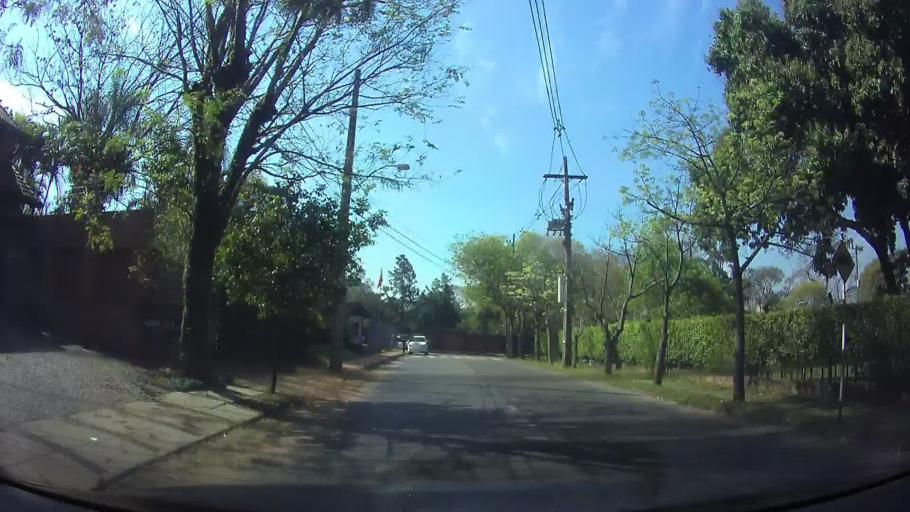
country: PY
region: Central
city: Fernando de la Mora
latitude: -25.2835
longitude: -57.5533
